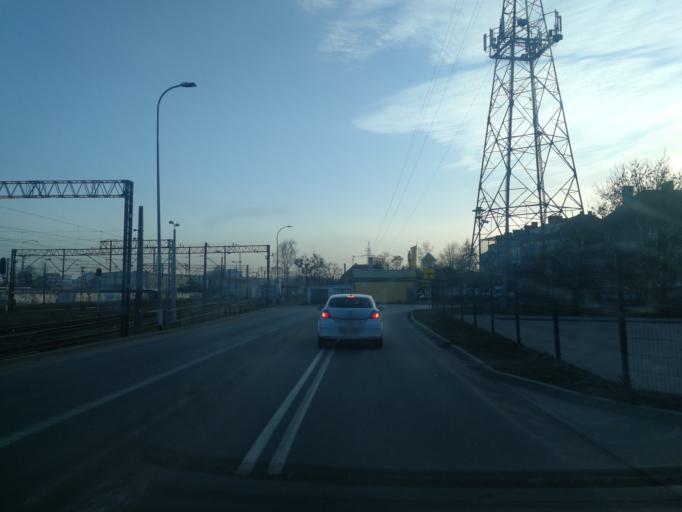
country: PL
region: Pomeranian Voivodeship
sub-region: Gdansk
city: Gdansk
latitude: 54.3870
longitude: 18.6312
